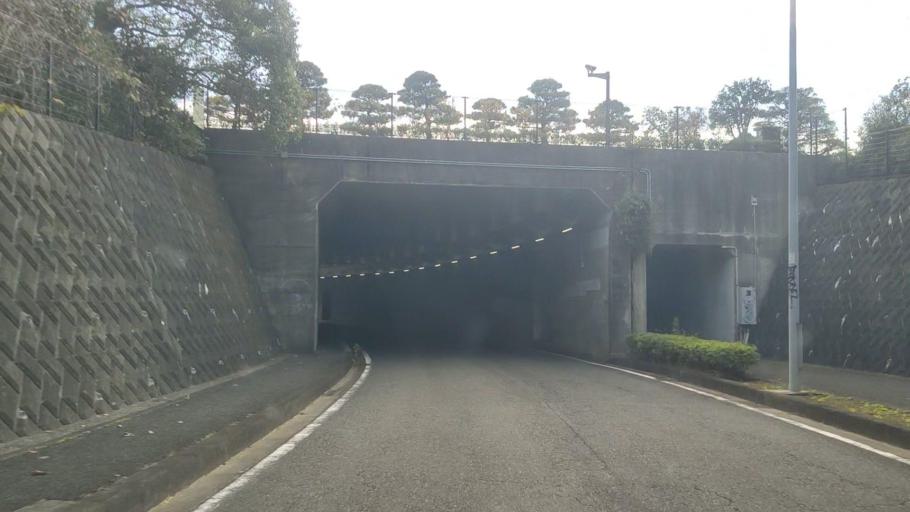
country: JP
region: Kanagawa
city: Yokohama
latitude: 35.4461
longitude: 139.5497
